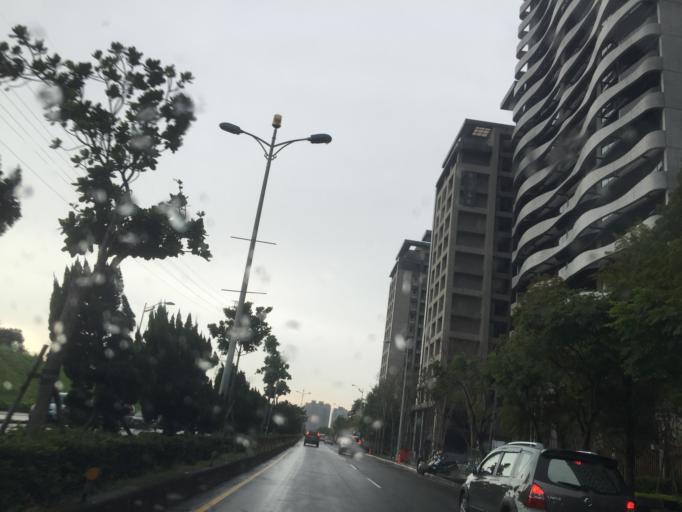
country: TW
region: Taiwan
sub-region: Hsinchu
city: Zhubei
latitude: 24.8200
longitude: 121.0079
